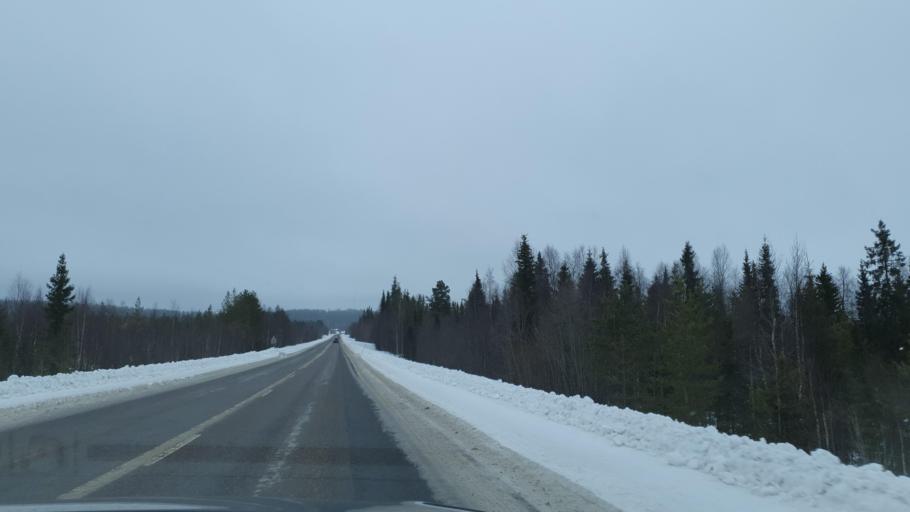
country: FI
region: Lapland
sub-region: Torniolaakso
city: Pello
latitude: 67.0796
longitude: 24.0137
